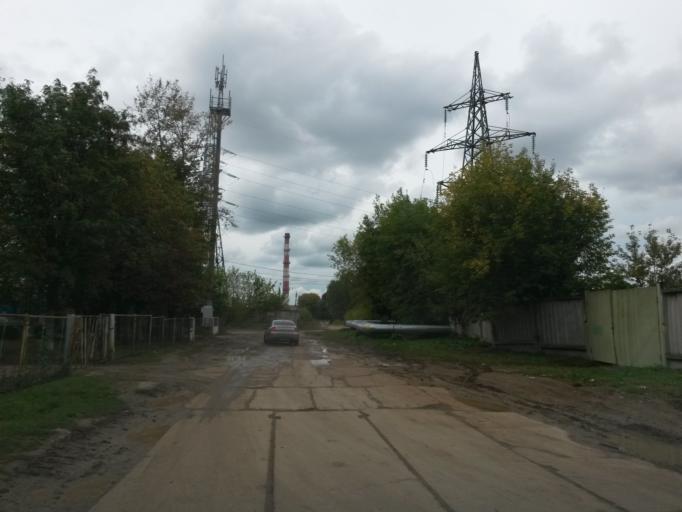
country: RU
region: Moskovskaya
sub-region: Chekhovskiy Rayon
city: Chekhov
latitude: 55.1449
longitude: 37.4799
